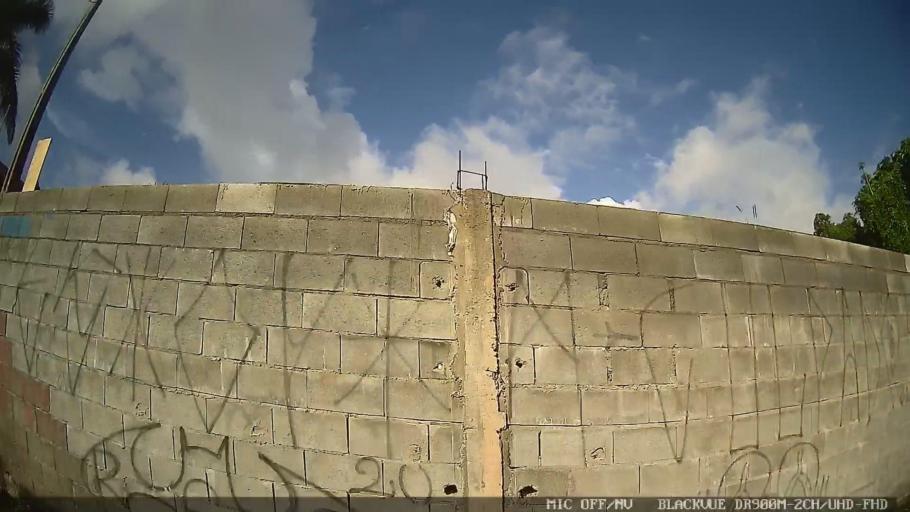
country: BR
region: Sao Paulo
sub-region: Itanhaem
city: Itanhaem
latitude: -24.1999
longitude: -46.8098
